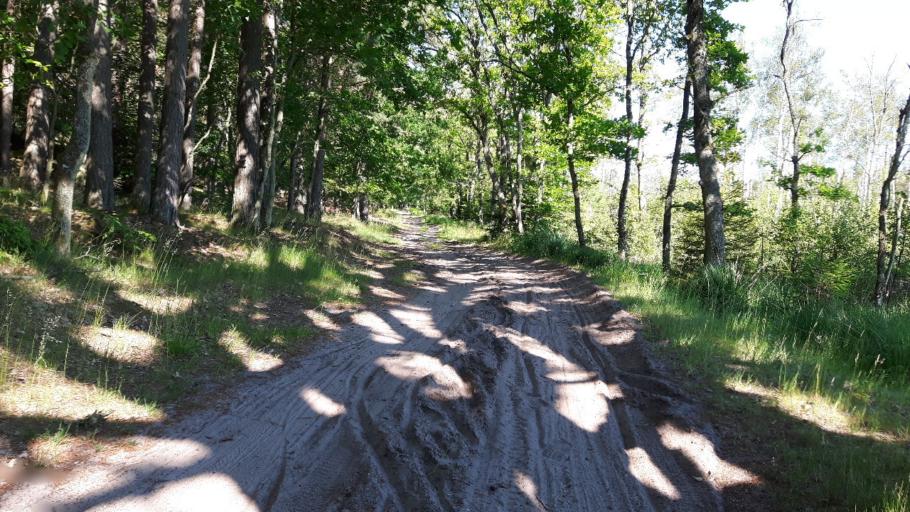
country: PL
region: Pomeranian Voivodeship
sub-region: Powiat leborski
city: Leba
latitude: 54.6990
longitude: 17.4907
